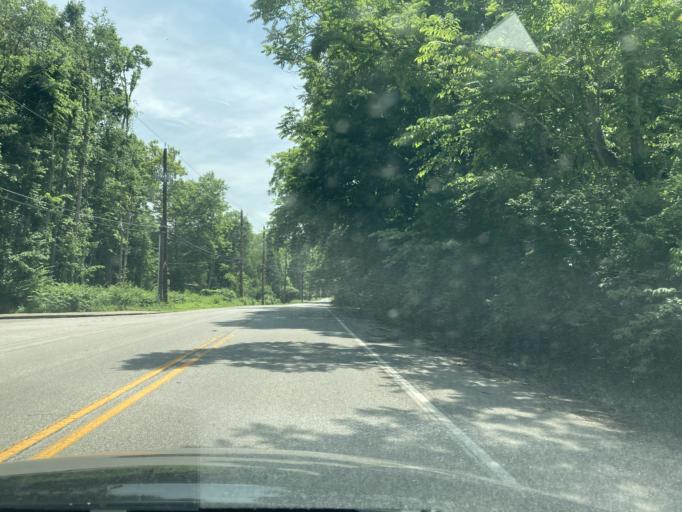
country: US
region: Indiana
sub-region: Marion County
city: Meridian Hills
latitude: 39.8637
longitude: -86.1723
